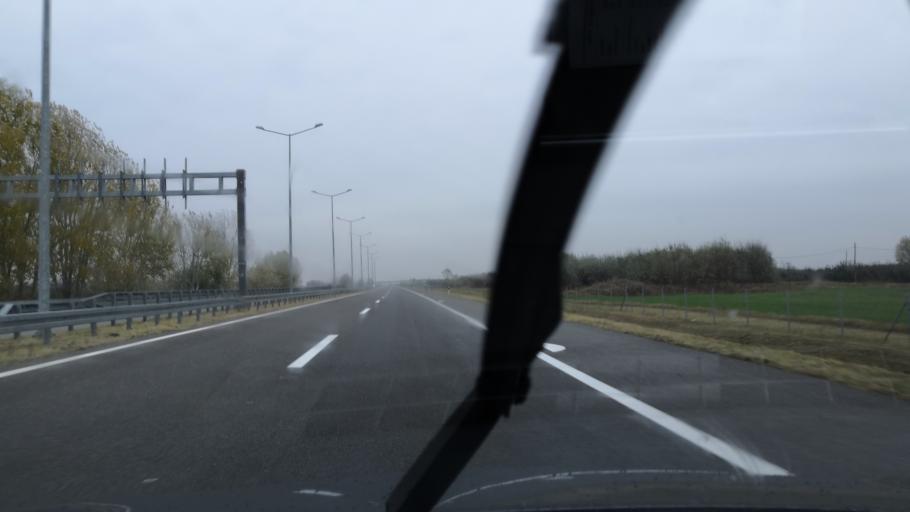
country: HU
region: Csongrad
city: Morahalom
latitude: 46.1324
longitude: 19.8732
